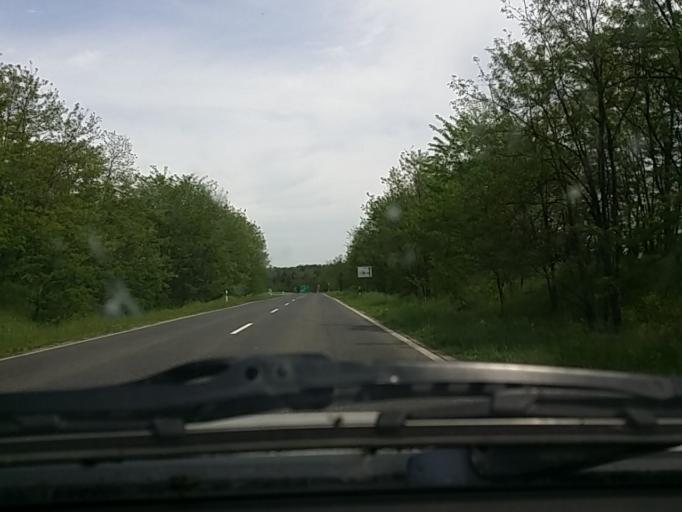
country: HU
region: Somogy
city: Barcs
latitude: 45.9619
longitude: 17.4946
